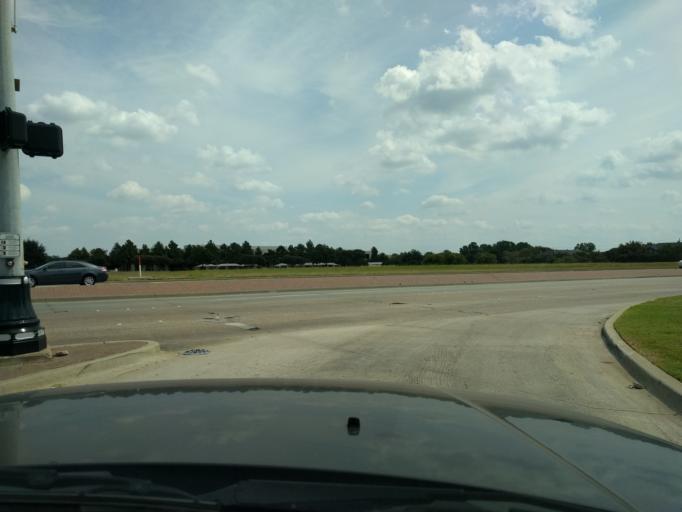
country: US
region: Texas
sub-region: Dallas County
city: Addison
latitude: 33.0188
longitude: -96.8437
